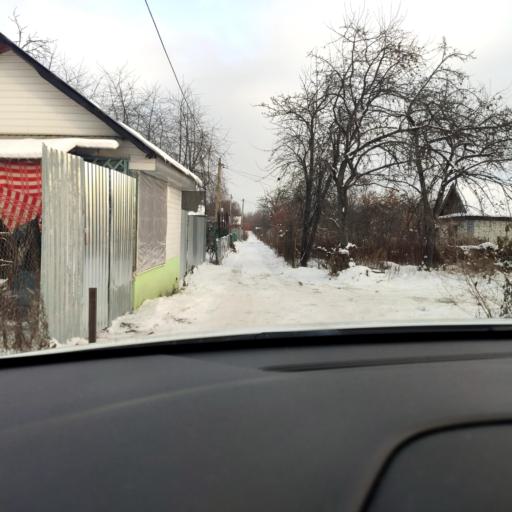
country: RU
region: Tatarstan
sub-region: Gorod Kazan'
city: Kazan
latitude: 55.8434
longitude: 49.0889
